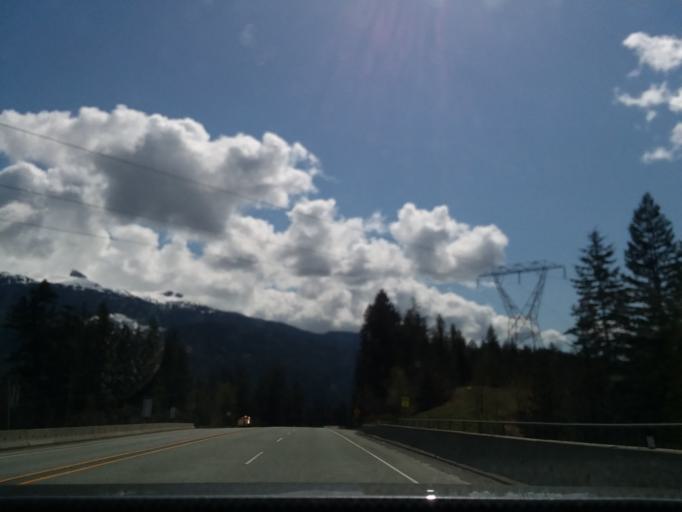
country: CA
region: British Columbia
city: Whistler
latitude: 50.0330
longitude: -123.1232
